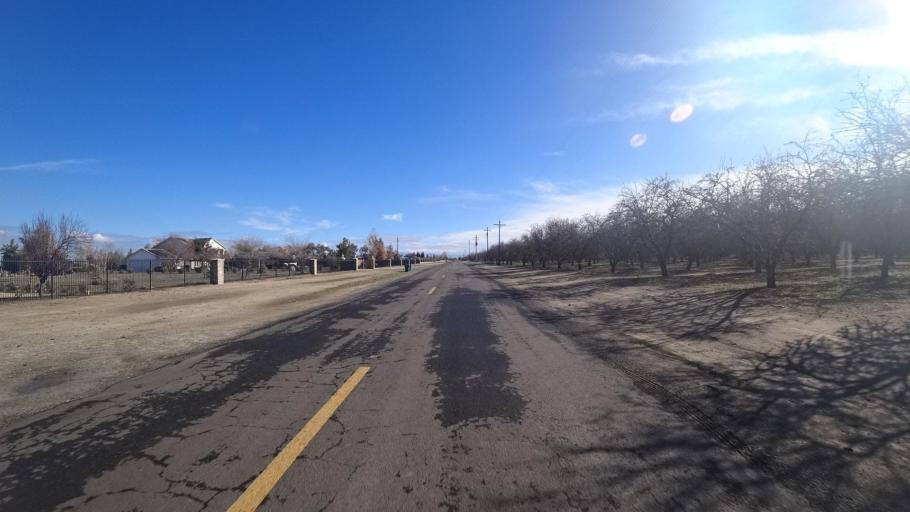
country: US
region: California
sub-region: Kern County
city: Rosedale
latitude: 35.3687
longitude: -119.2275
